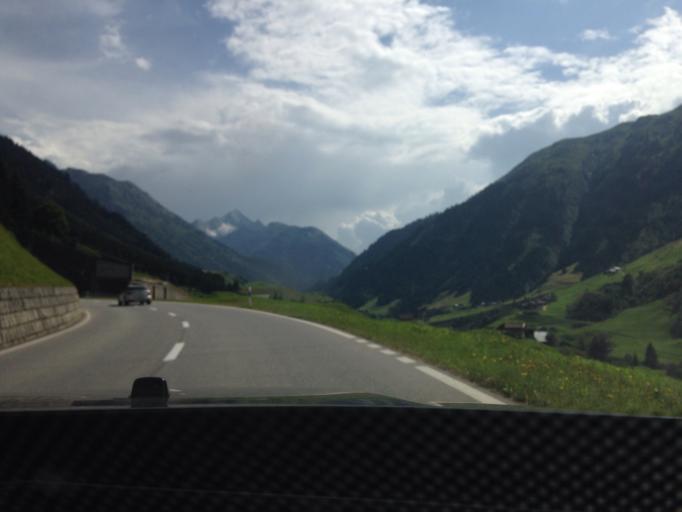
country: CH
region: Grisons
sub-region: Surselva District
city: Disentis
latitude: 46.6646
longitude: 8.8578
